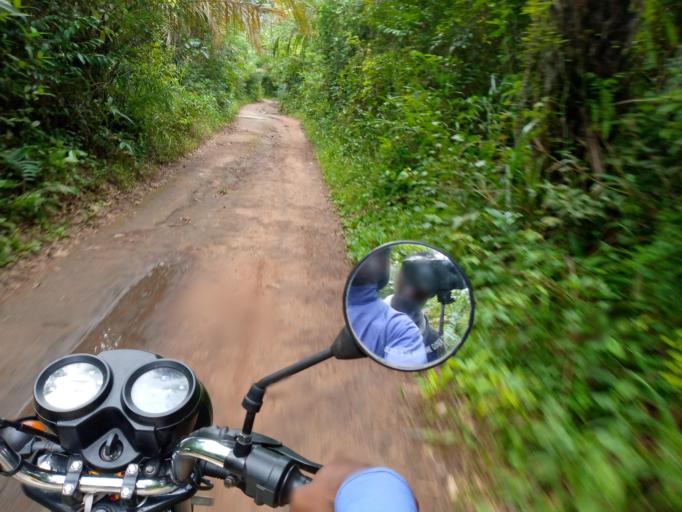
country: SL
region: Northern Province
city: Mange
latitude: 8.9796
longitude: -12.8196
